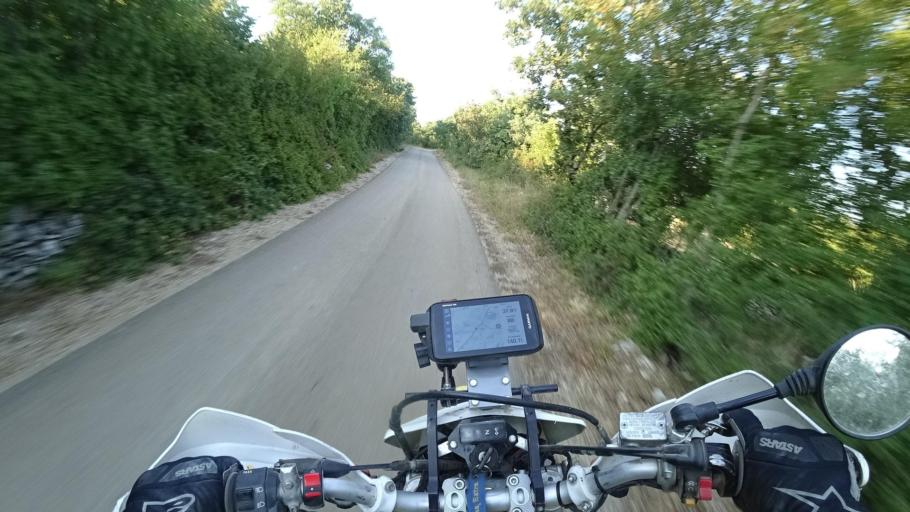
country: HR
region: Istarska
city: Vodnjan
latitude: 44.9889
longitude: 13.9015
